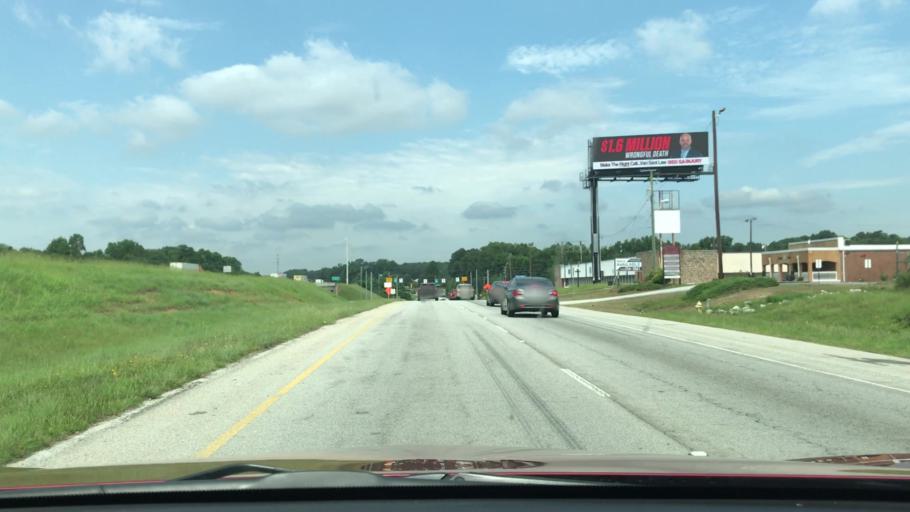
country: US
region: Georgia
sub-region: DeKalb County
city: Lithonia
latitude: 33.7036
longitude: -84.1279
